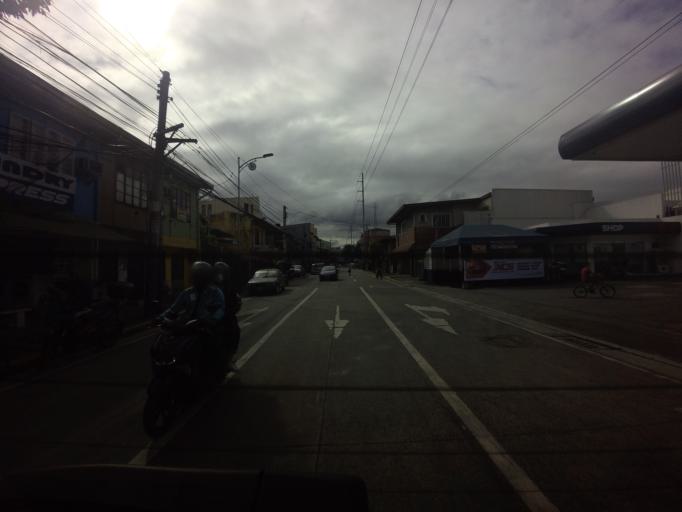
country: PH
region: Metro Manila
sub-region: City of Manila
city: Quiapo
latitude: 14.6050
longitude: 121.0004
